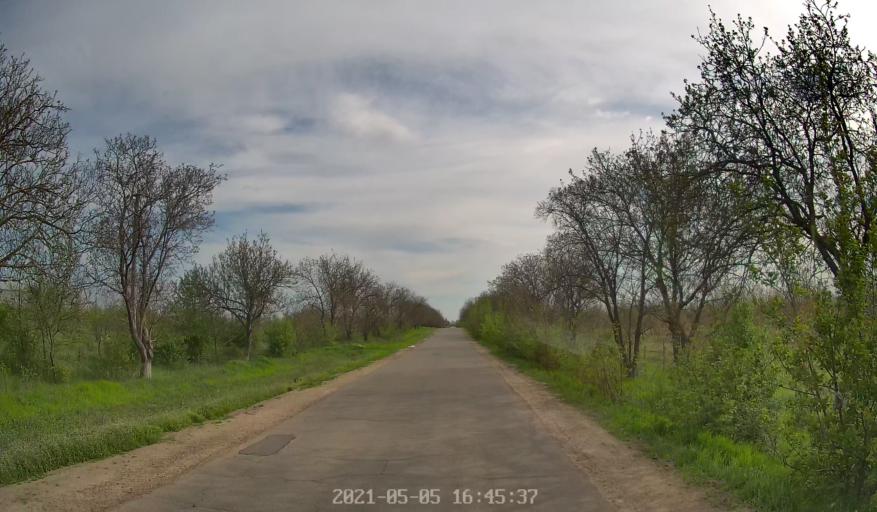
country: MD
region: Criuleni
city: Criuleni
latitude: 47.1079
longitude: 29.1931
